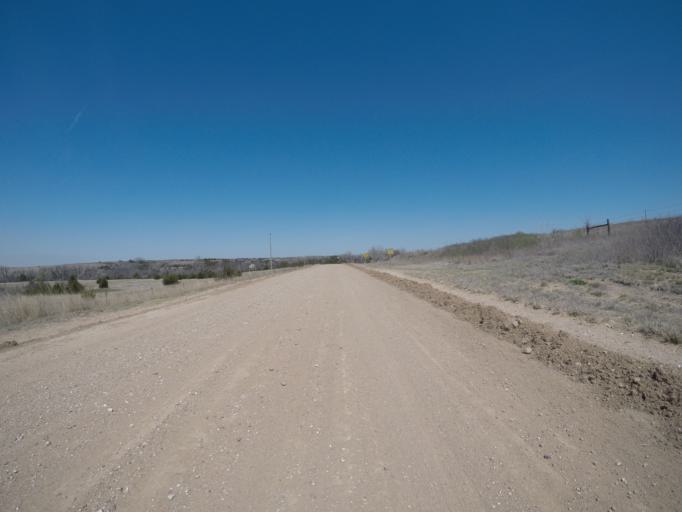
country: US
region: Kansas
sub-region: Pratt County
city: Pratt
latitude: 37.3992
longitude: -98.8378
